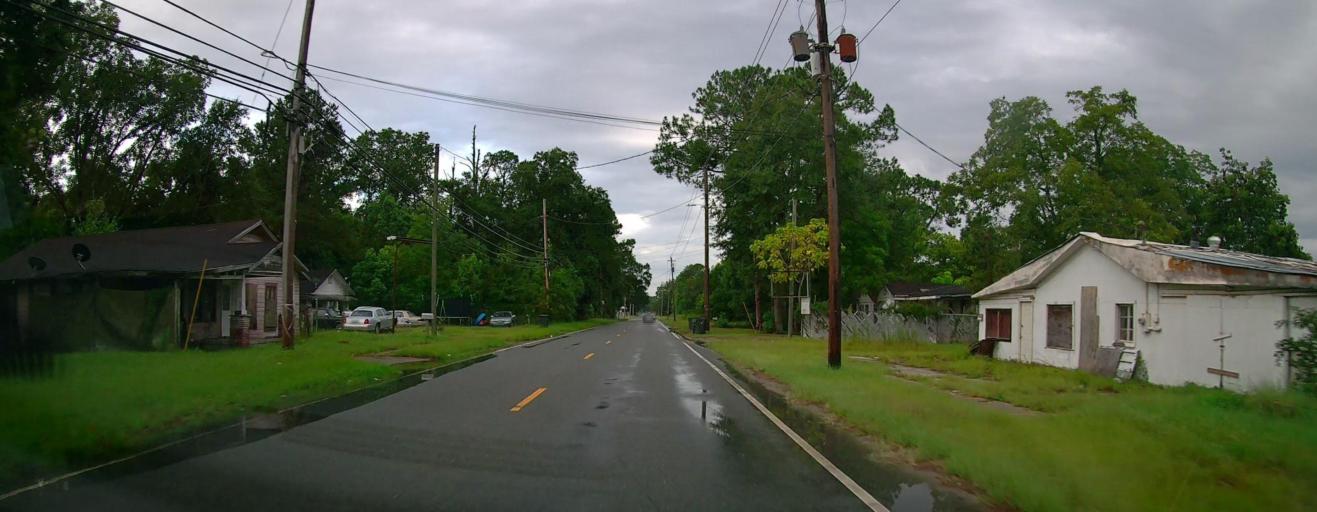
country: US
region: Georgia
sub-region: Ware County
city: Waycross
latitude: 31.2013
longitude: -82.3717
